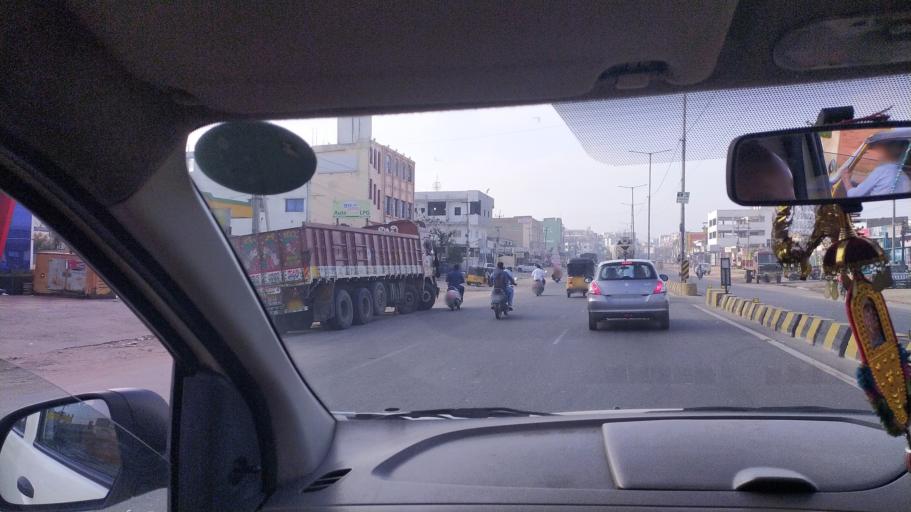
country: IN
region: Telangana
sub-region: Rangareddi
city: Balapur
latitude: 17.3200
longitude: 78.4672
